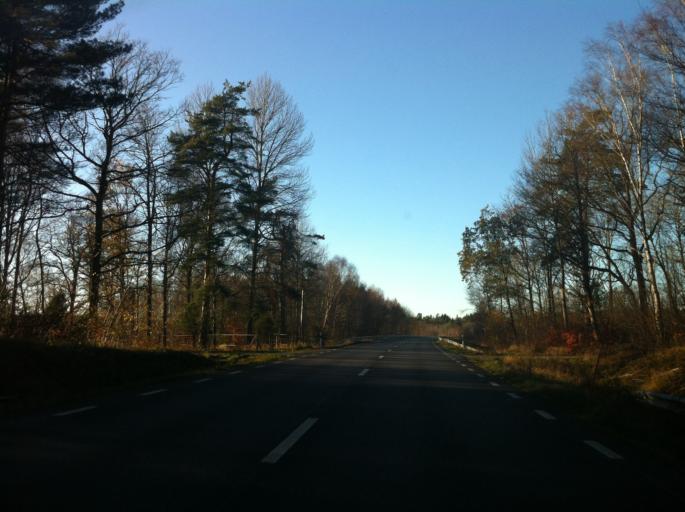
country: SE
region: Blekinge
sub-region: Karlshamns Kommun
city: Morrum
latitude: 56.1732
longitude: 14.6494
